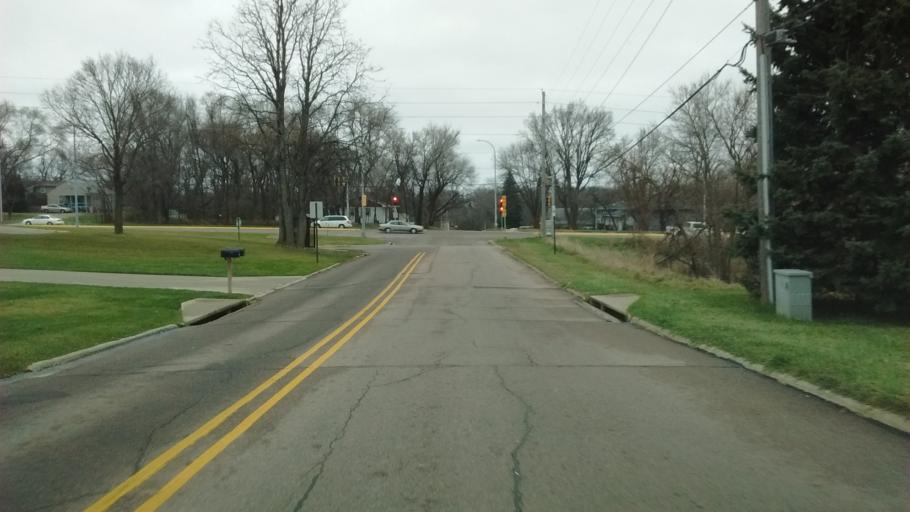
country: US
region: Iowa
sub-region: Woodbury County
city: Sioux City
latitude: 42.4766
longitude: -96.3396
